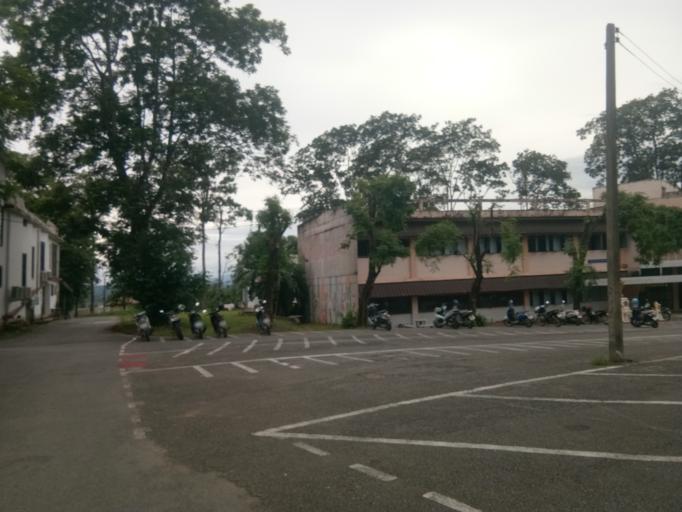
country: TH
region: Chiang Rai
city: Chiang Rai
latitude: 19.9804
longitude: 99.8493
